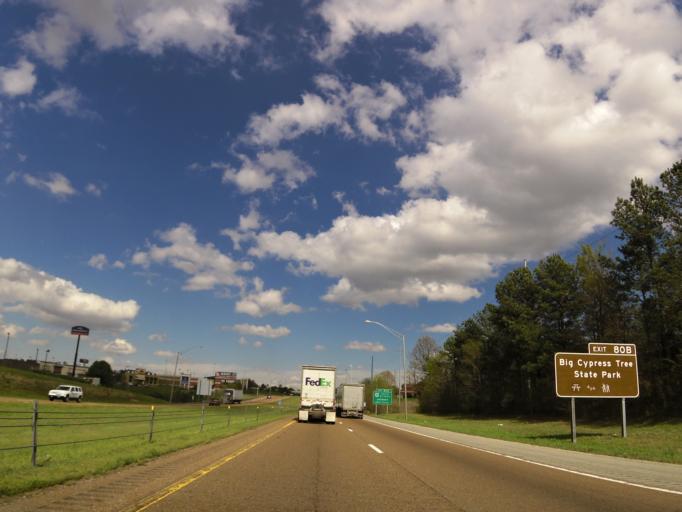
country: US
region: Tennessee
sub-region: Madison County
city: Jackson
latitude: 35.6612
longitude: -88.8614
